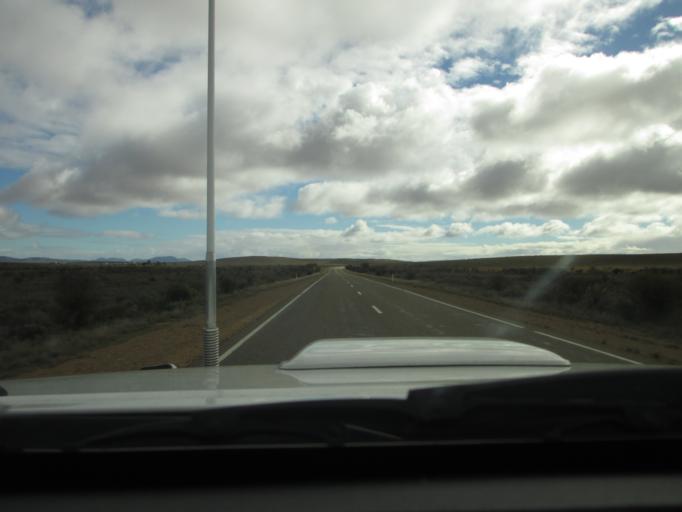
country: AU
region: South Australia
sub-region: Flinders Ranges
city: Quorn
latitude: -32.1097
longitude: 138.5034
